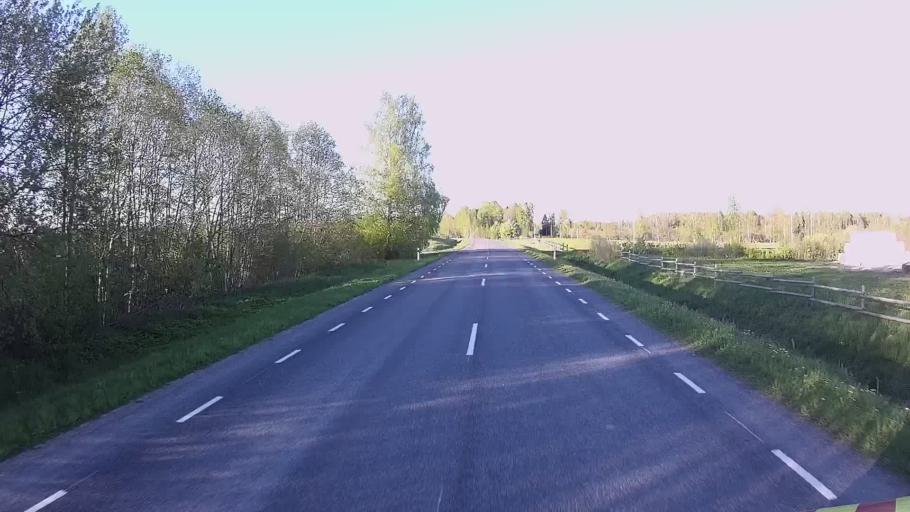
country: EE
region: Jogevamaa
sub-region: Poltsamaa linn
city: Poltsamaa
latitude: 58.5153
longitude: 25.8611
